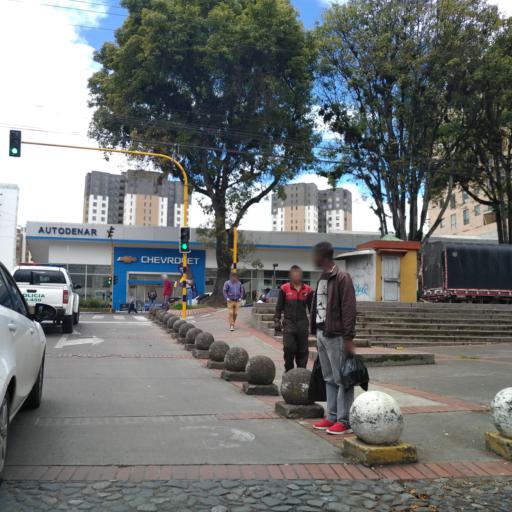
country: CO
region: Narino
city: Pasto
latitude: 1.2144
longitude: -77.2754
